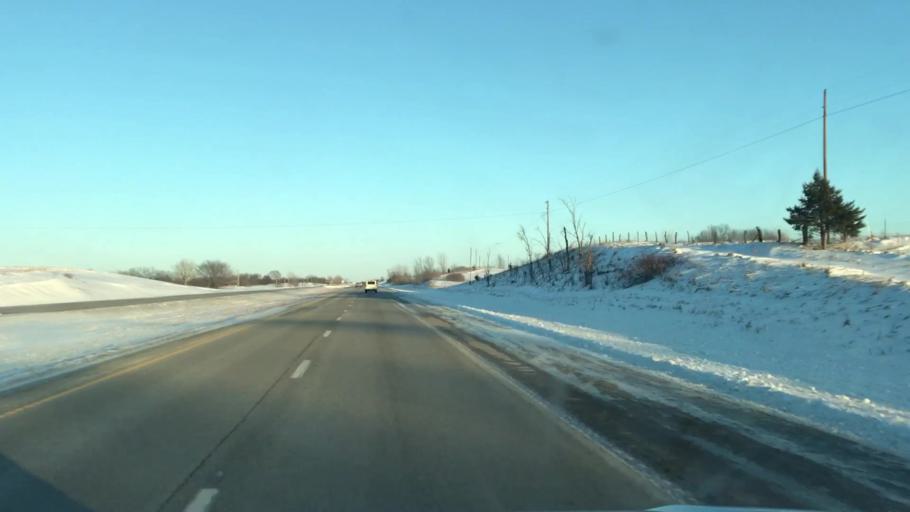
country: US
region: Missouri
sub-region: Clinton County
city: Gower
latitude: 39.7471
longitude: -94.6318
